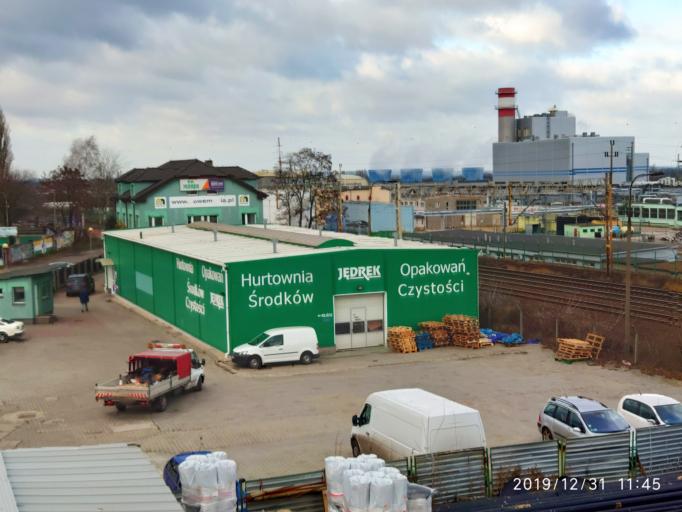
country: PL
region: Lubusz
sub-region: Zielona Gora
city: Zielona Gora
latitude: 51.9487
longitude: 15.4921
